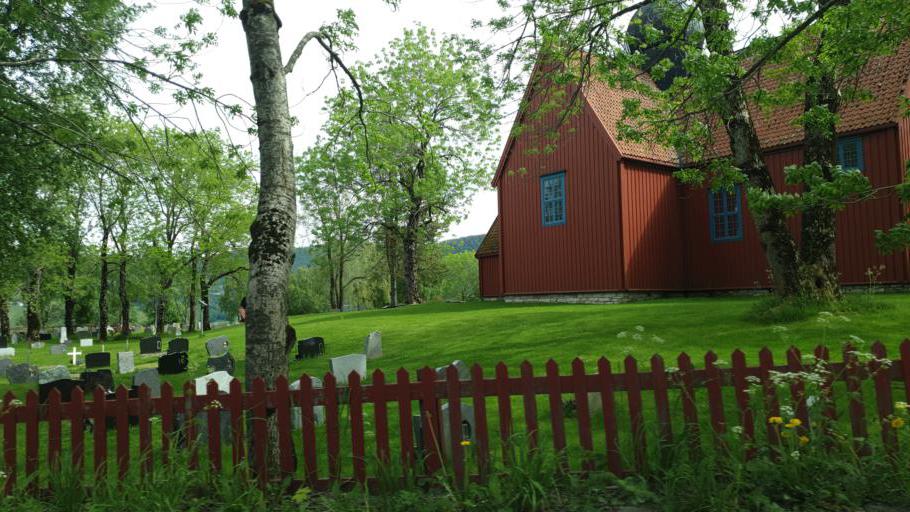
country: NO
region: Sor-Trondelag
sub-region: Rissa
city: Rissa
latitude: 63.5649
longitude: 9.9255
